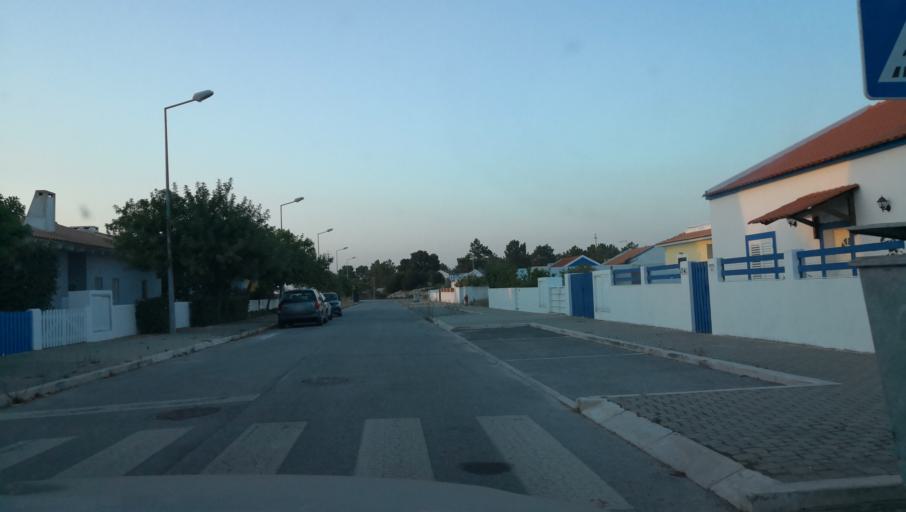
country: PT
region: Setubal
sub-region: Setubal
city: Setubal
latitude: 38.3976
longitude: -8.7725
